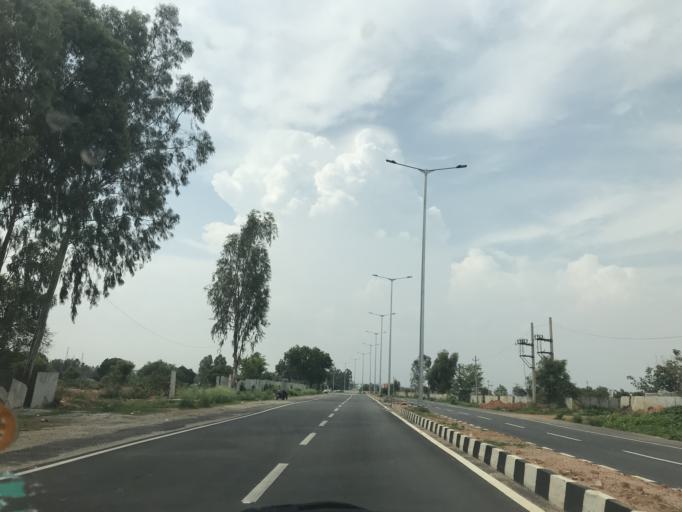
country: IN
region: Karnataka
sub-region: Bangalore Urban
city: Yelahanka
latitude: 13.1153
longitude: 77.6680
